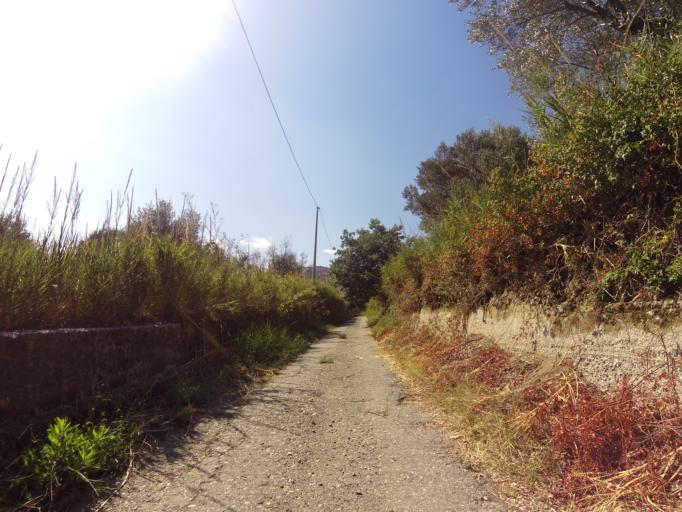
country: IT
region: Calabria
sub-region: Provincia di Reggio Calabria
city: Pazzano
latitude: 38.4594
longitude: 16.4572
